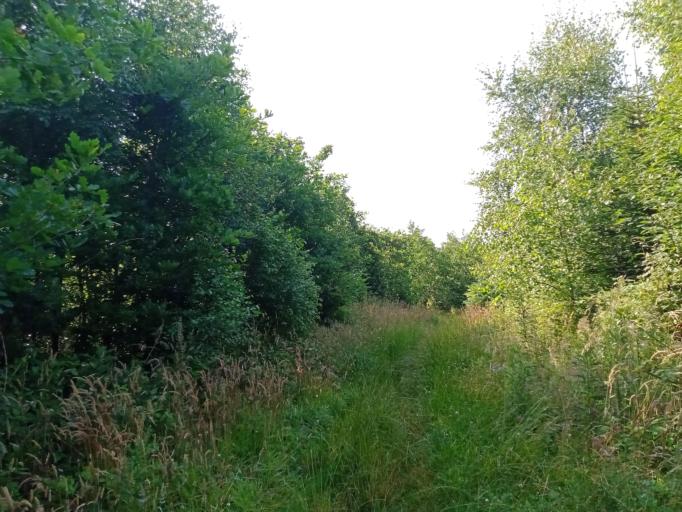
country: IE
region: Leinster
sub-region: Laois
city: Abbeyleix
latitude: 52.9054
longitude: -7.3565
